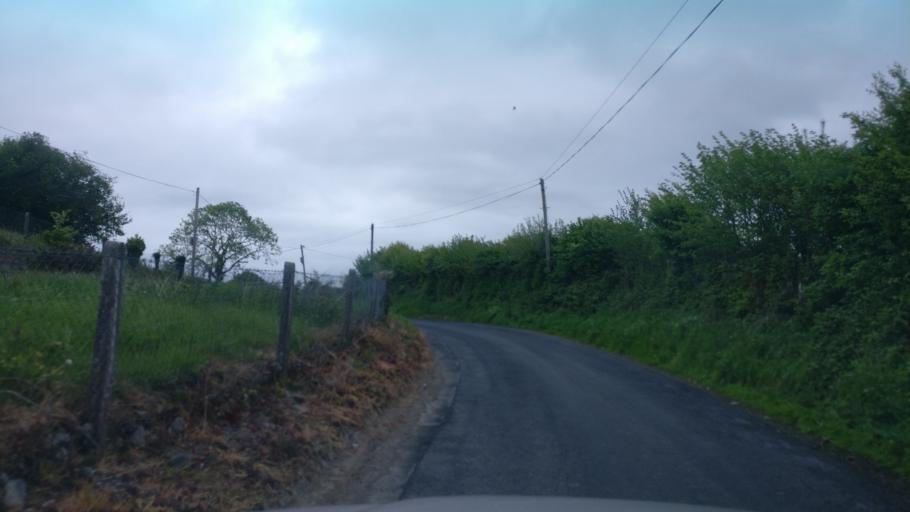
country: IE
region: Connaught
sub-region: County Galway
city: Portumna
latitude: 53.1414
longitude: -8.2893
